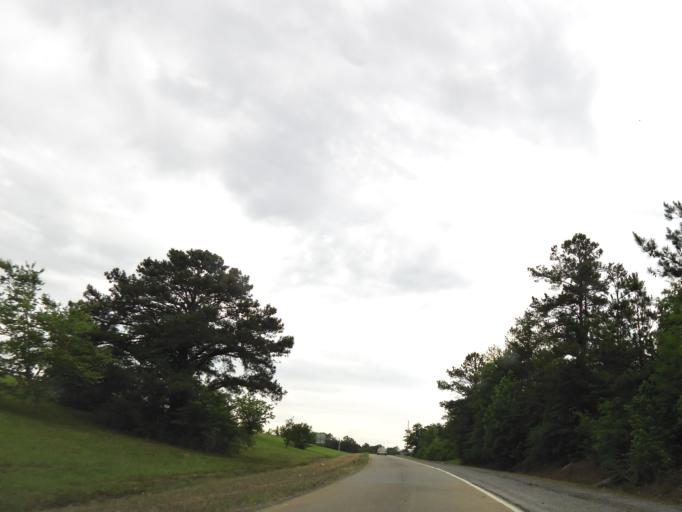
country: US
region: Georgia
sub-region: Bibb County
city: West Point
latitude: 32.8113
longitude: -83.7257
